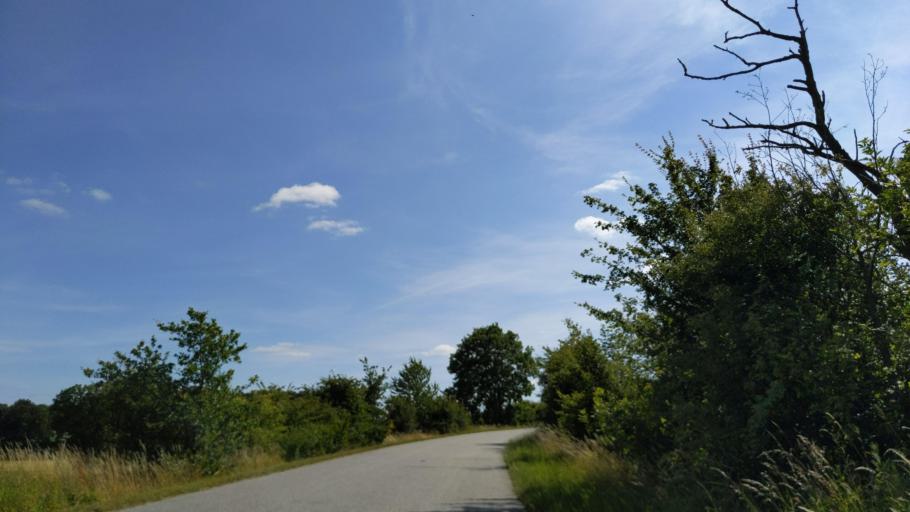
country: DE
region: Schleswig-Holstein
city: Kasseedorf
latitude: 54.1342
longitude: 10.7433
